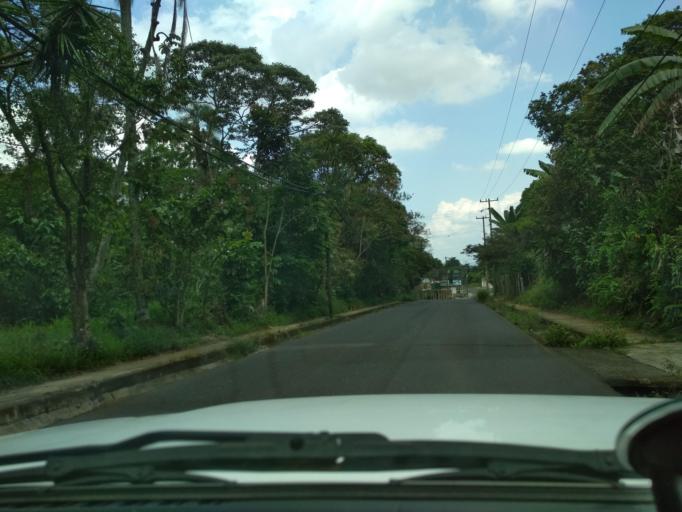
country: MX
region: Veracruz
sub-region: Cordoba
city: San Jose de Abajo [Unidad Habitacional]
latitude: 18.9190
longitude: -96.9614
